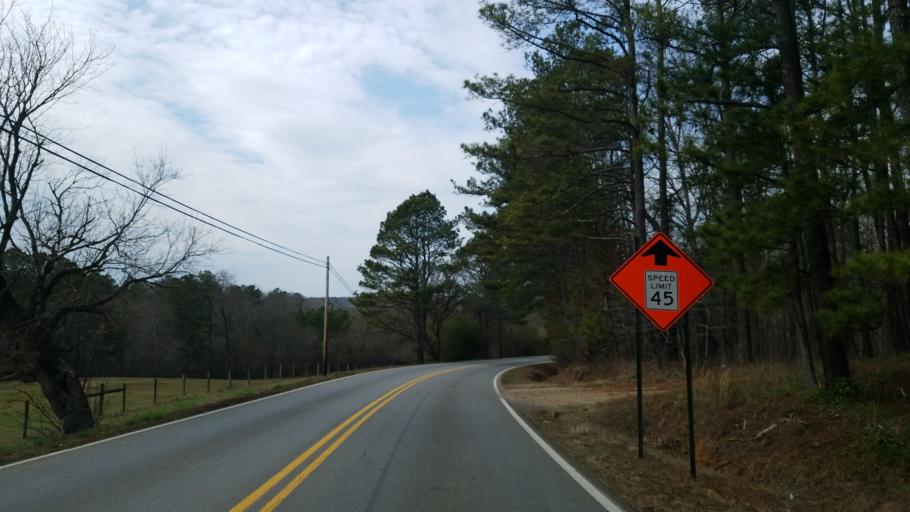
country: US
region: Georgia
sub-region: Cherokee County
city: Ball Ground
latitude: 34.3123
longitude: -84.3416
